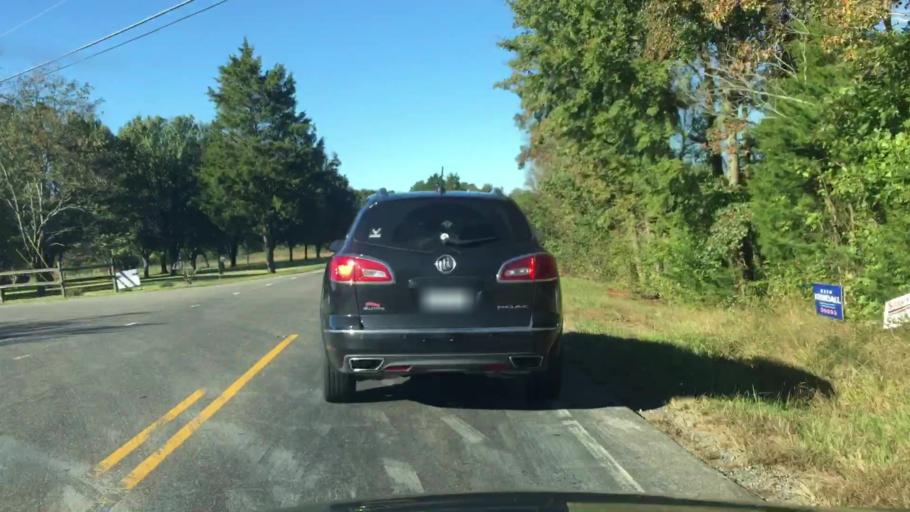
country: US
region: North Carolina
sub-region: Gaston County
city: Davidson
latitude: 35.5193
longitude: -80.7705
